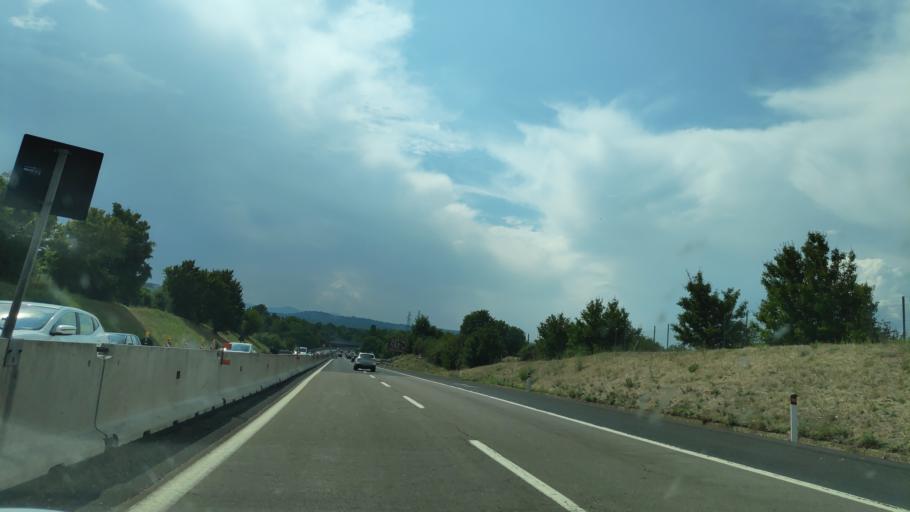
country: IT
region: Tuscany
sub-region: Province of Arezzo
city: Ponticino
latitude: 43.4841
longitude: 11.7179
